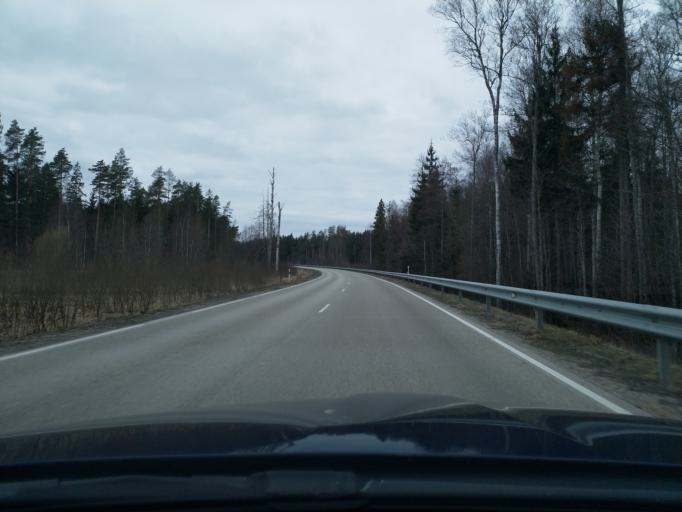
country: LV
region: Talsu Rajons
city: Sabile
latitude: 56.9532
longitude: 22.2981
